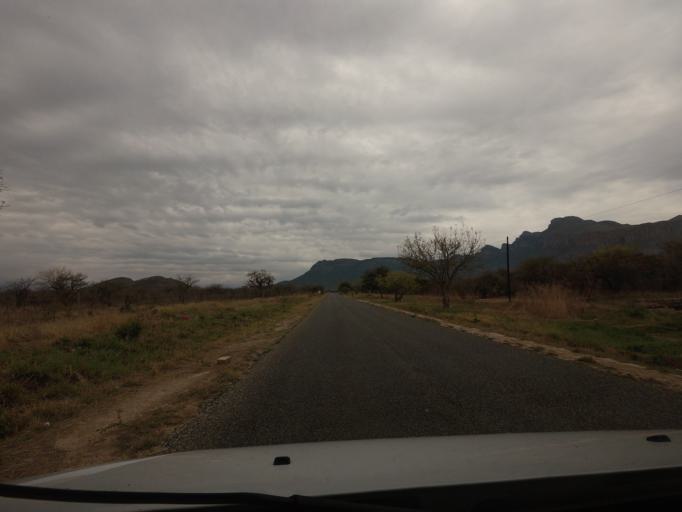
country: ZA
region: Limpopo
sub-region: Mopani District Municipality
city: Hoedspruit
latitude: -24.4916
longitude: 30.8909
